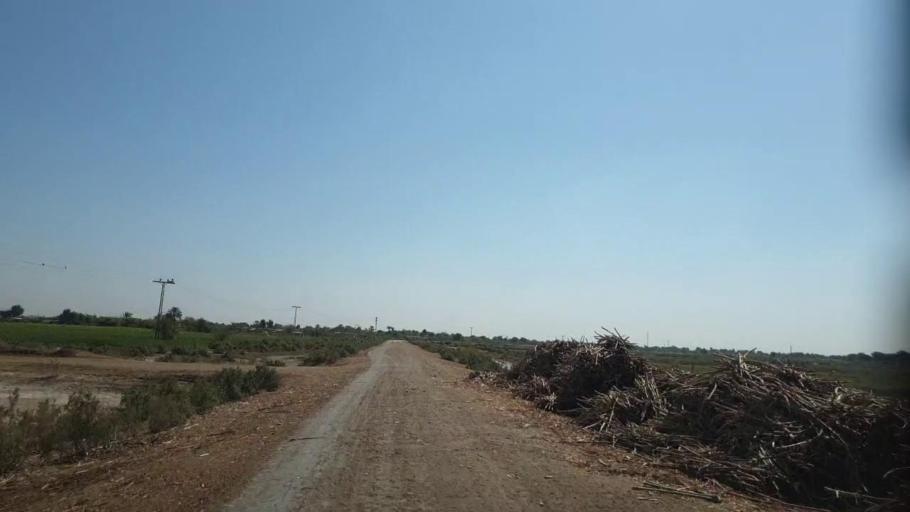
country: PK
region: Sindh
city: Mirpur Khas
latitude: 25.5854
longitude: 69.1098
